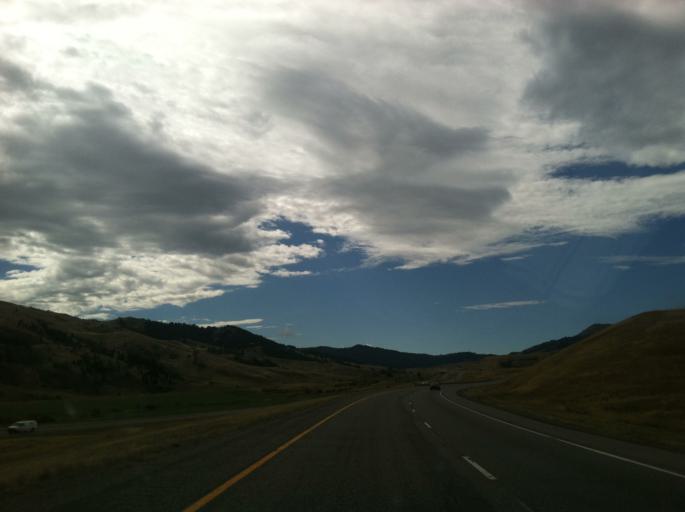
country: US
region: Montana
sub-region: Park County
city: Livingston
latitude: 45.6632
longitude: -110.7026
